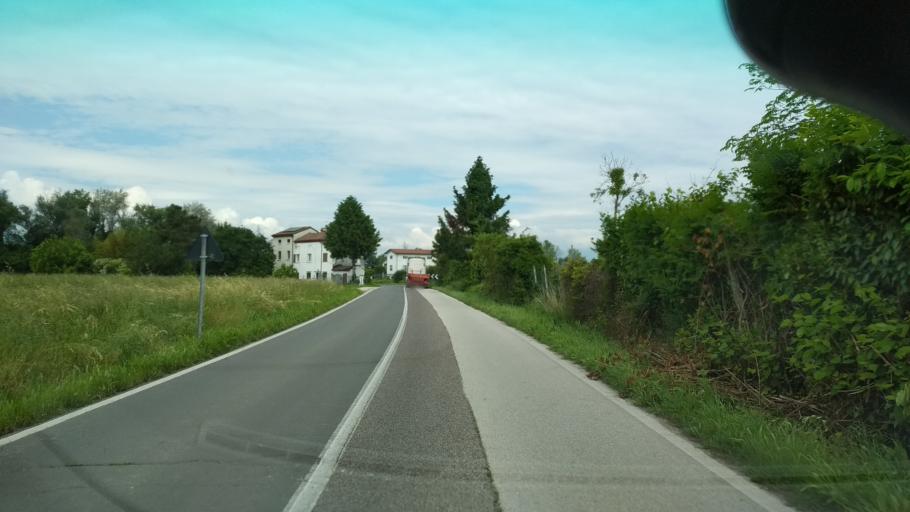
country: IT
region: Veneto
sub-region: Provincia di Vicenza
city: Monticello Conte Otto
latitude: 45.5978
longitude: 11.5500
